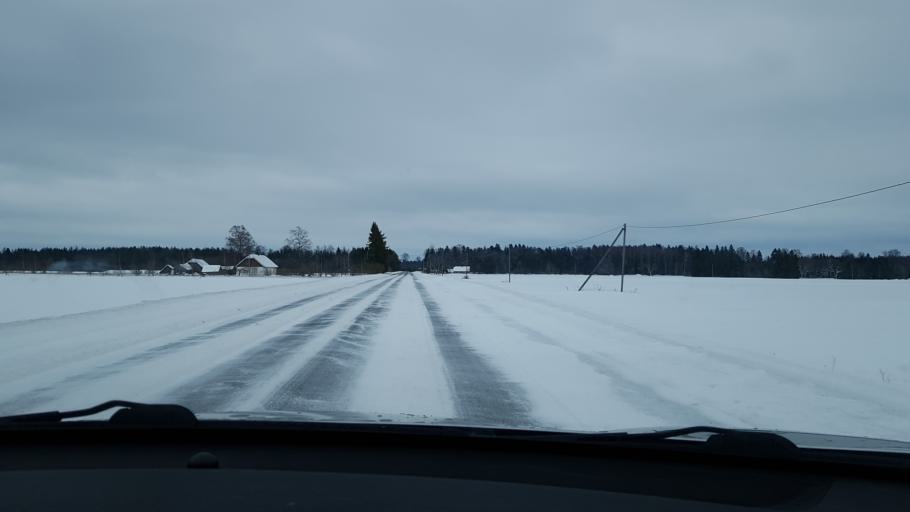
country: EE
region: Jaervamaa
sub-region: Jaerva-Jaani vald
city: Jarva-Jaani
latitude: 59.1087
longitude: 25.8016
